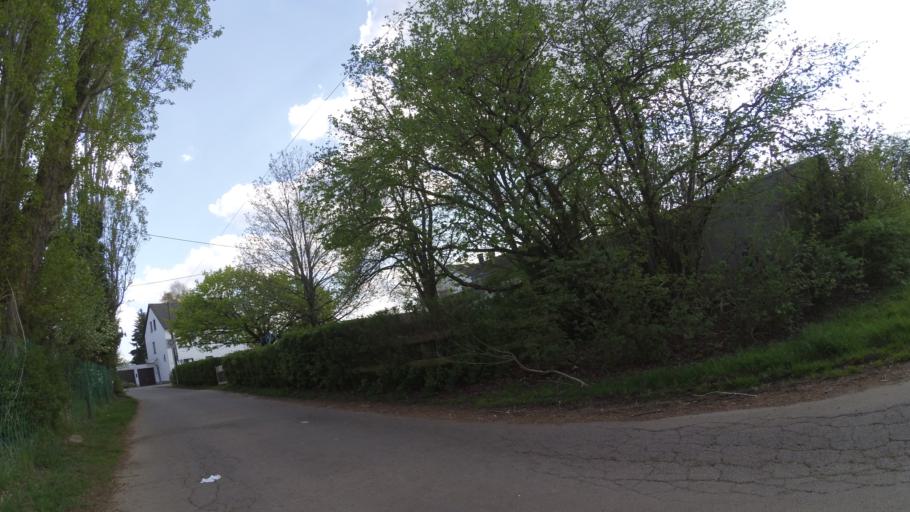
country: DE
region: Saarland
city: Riegelsberg
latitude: 49.3177
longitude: 6.9292
